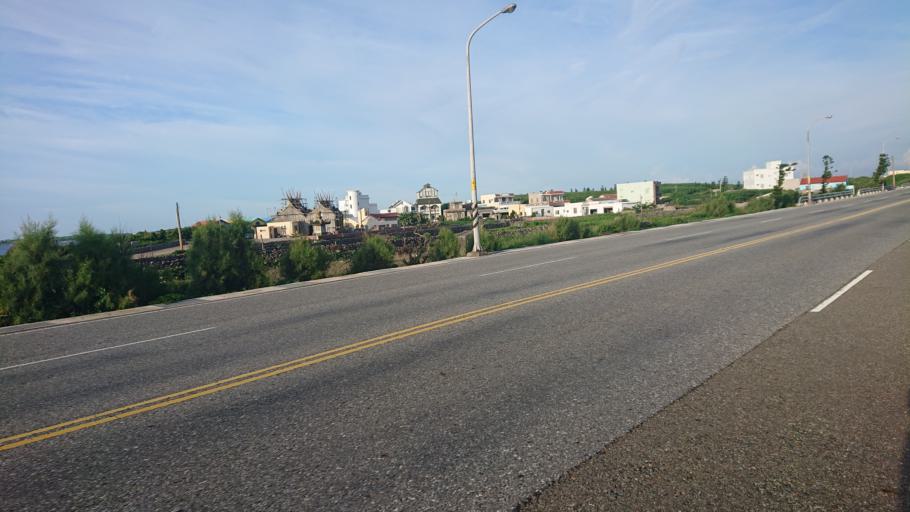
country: TW
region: Taiwan
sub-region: Penghu
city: Ma-kung
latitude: 23.6368
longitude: 119.5330
